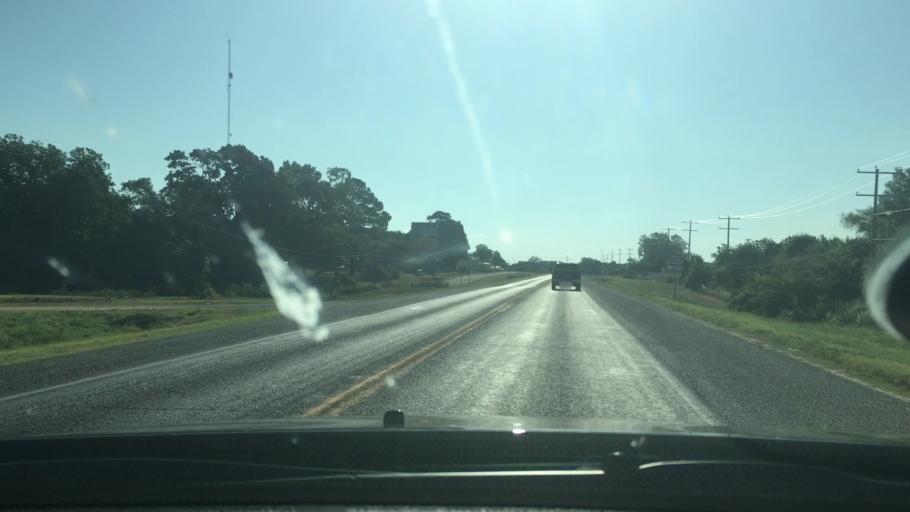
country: US
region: Oklahoma
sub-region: Johnston County
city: Tishomingo
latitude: 34.2370
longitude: -96.7059
